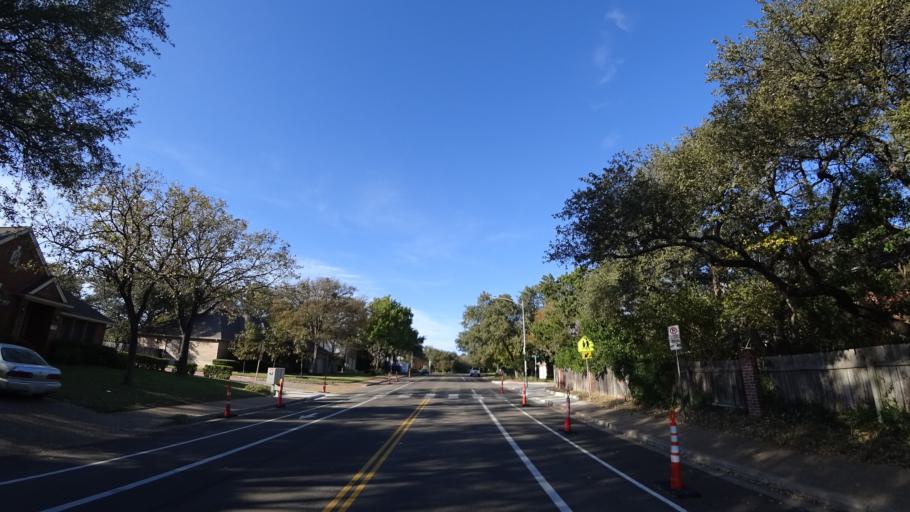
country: US
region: Texas
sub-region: Williamson County
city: Jollyville
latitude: 30.4136
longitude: -97.7791
